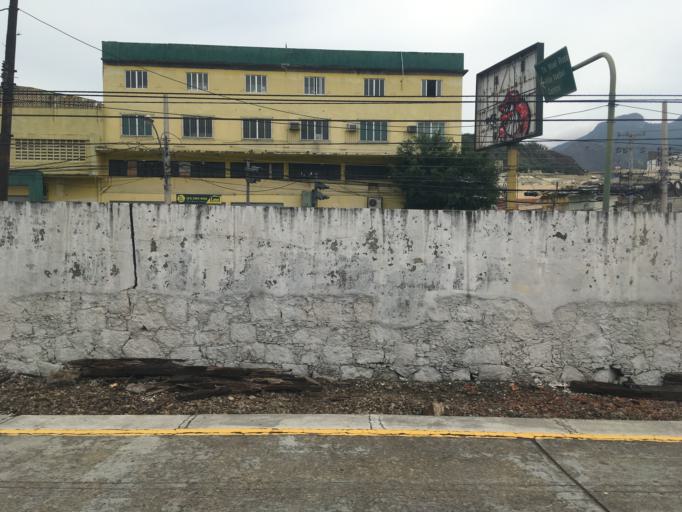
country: BR
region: Rio de Janeiro
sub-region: Rio De Janeiro
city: Rio de Janeiro
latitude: -22.9021
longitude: -43.2636
